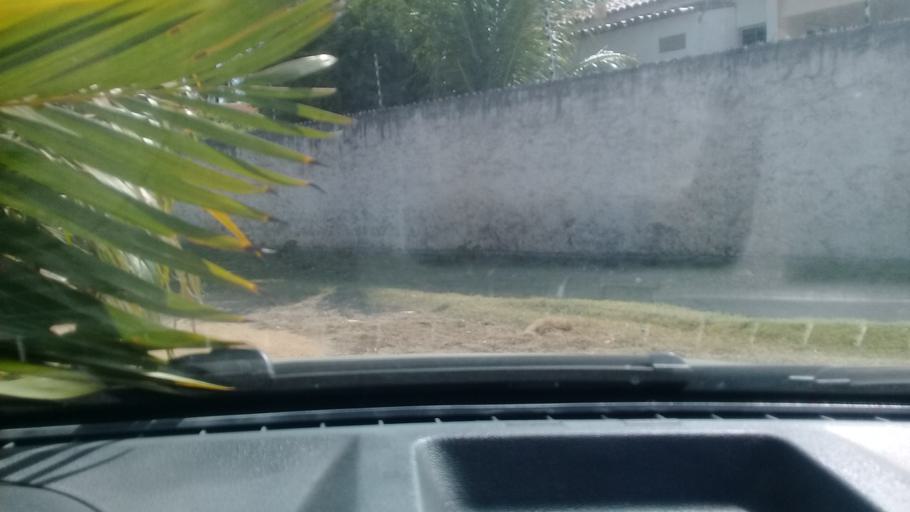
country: BR
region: Pernambuco
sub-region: Itamaraca
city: Itamaraca
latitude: -7.7967
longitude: -34.8388
